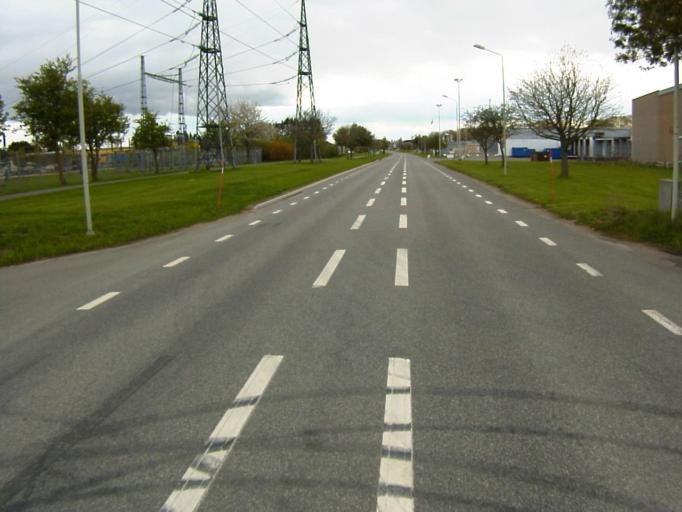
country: SE
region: Skane
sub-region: Kristianstads Kommun
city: Kristianstad
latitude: 56.0568
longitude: 14.1695
